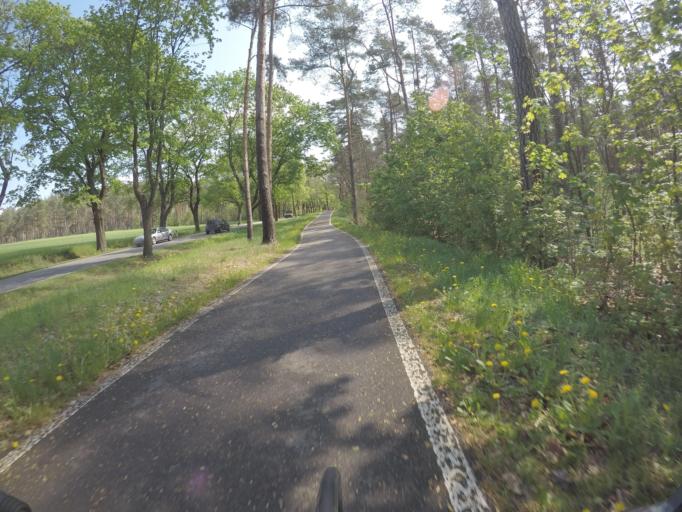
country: DE
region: Brandenburg
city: Wandlitz
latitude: 52.7971
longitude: 13.5059
